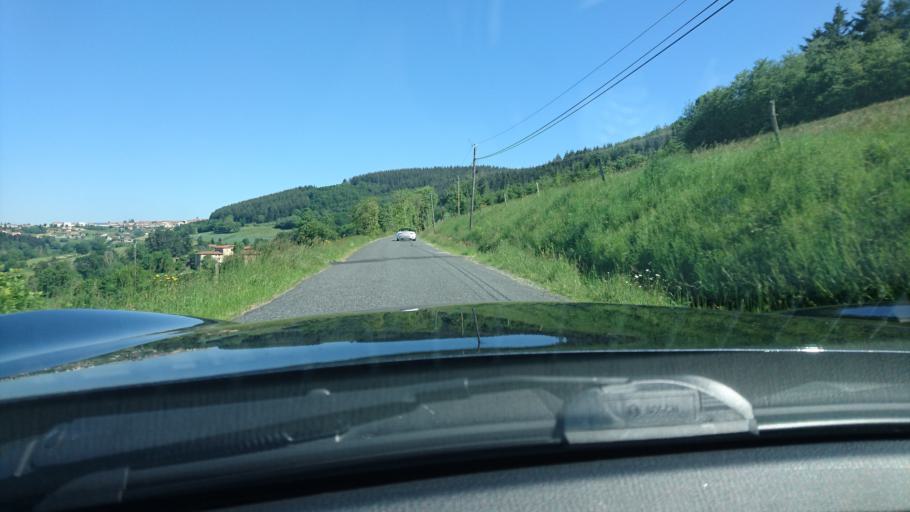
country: FR
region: Rhone-Alpes
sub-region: Departement de la Loire
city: Violay
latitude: 45.8347
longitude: 4.3707
